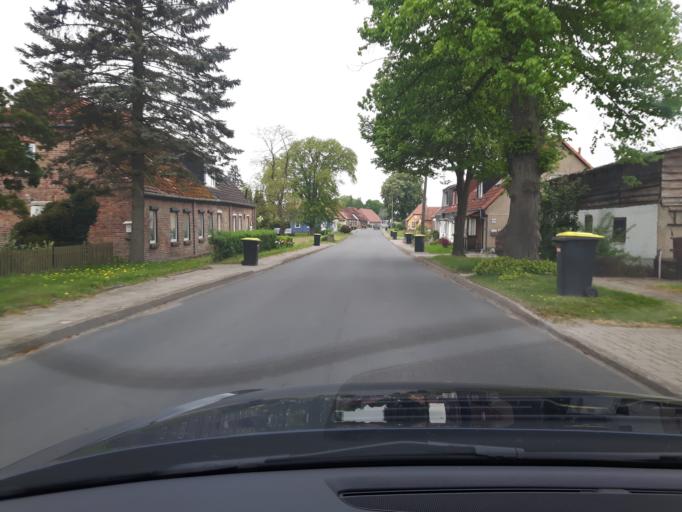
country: DE
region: Mecklenburg-Vorpommern
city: Gnoien
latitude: 54.0147
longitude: 12.6591
